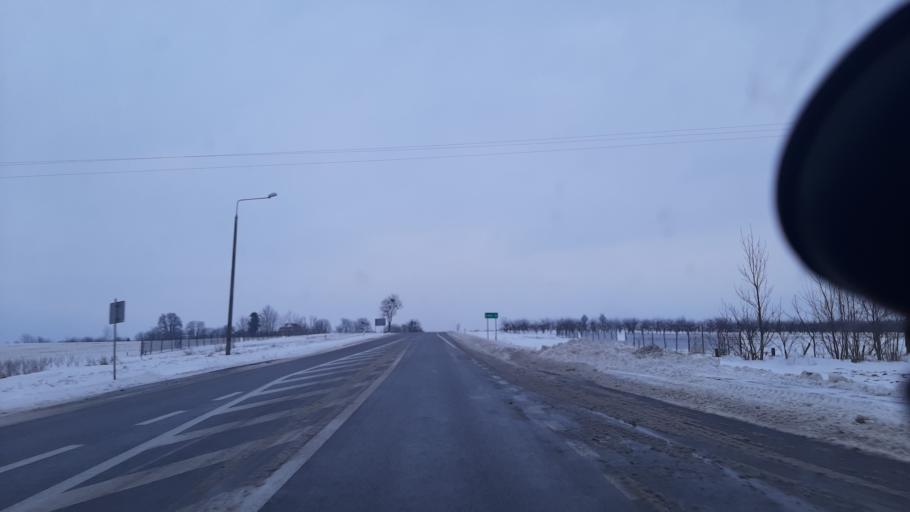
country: PL
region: Lublin Voivodeship
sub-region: Powiat pulawski
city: Markuszow
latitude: 51.3688
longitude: 22.2824
